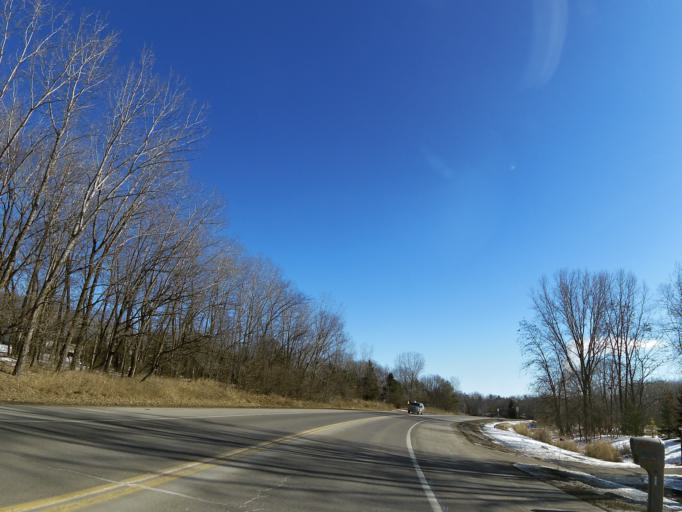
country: US
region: Minnesota
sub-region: Washington County
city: Stillwater
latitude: 45.0565
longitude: -92.8308
